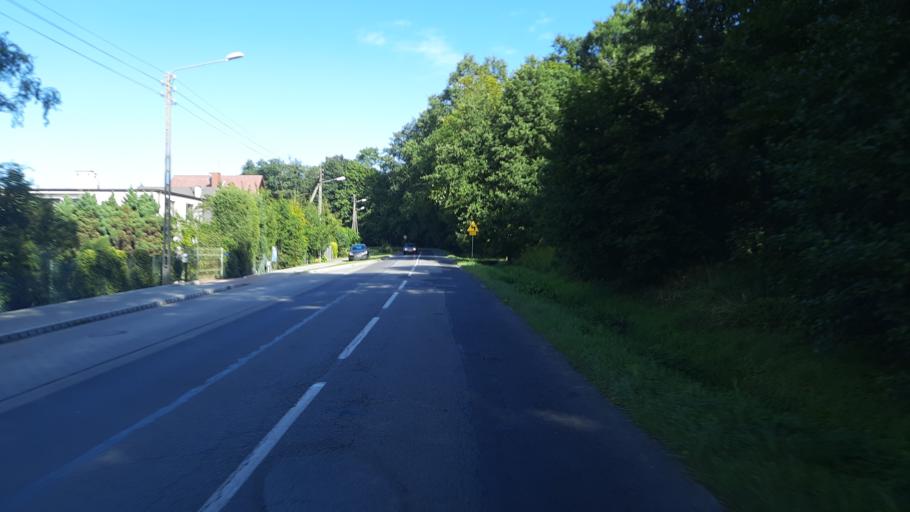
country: PL
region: Lower Silesian Voivodeship
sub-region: Powiat wroclawski
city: Dlugoleka
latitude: 51.1827
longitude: 17.1891
